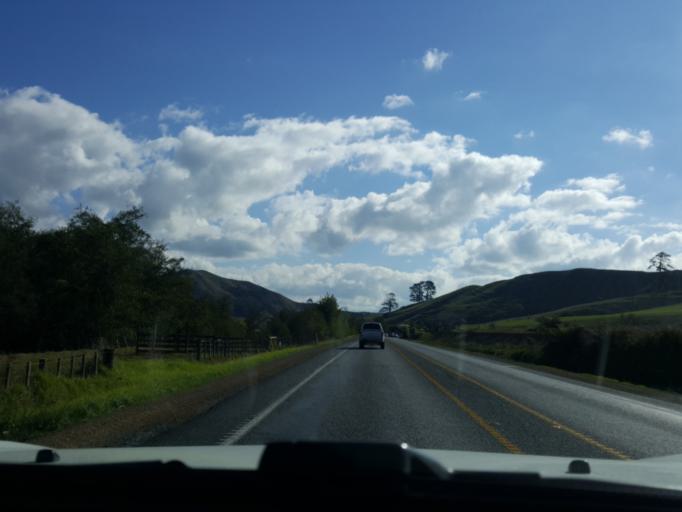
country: NZ
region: Waikato
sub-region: Waikato District
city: Ngaruawahia
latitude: -37.6049
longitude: 175.1763
